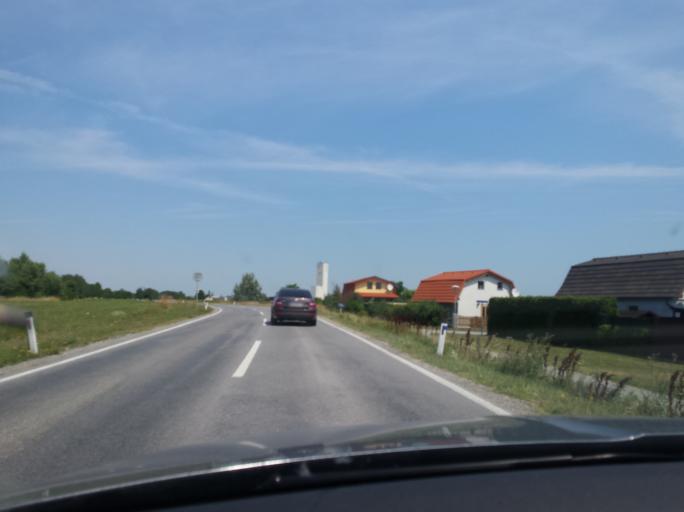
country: AT
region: Lower Austria
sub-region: Politischer Bezirk Bruck an der Leitha
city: Petronell-Carnuntum
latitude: 48.0984
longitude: 16.8634
